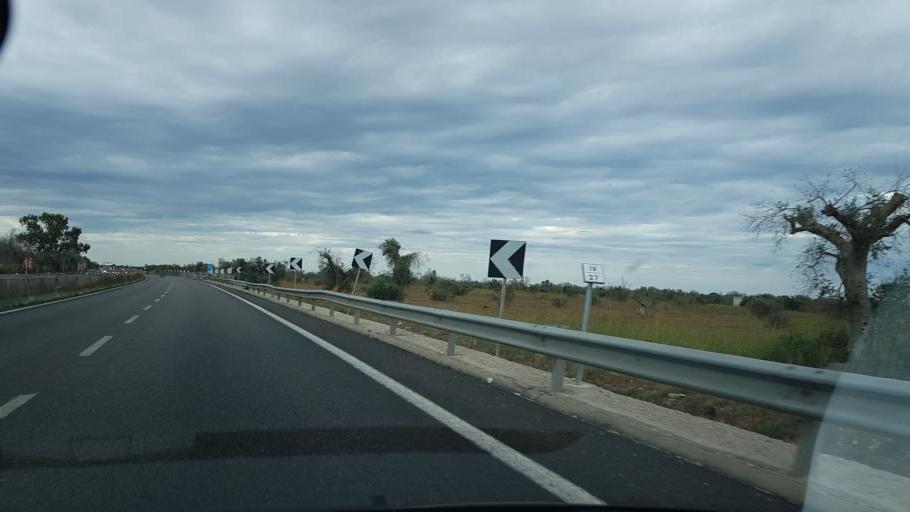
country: IT
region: Apulia
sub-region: Provincia di Lecce
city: Surbo
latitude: 40.4082
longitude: 18.1071
